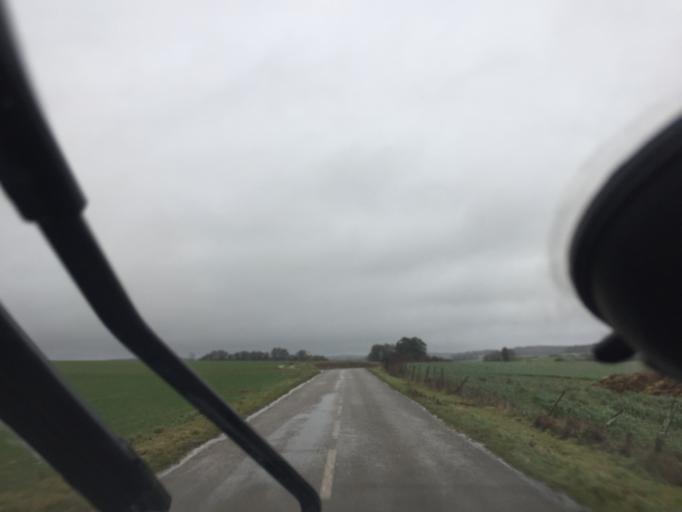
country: FR
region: Franche-Comte
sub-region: Departement du Jura
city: Orchamps
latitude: 47.1549
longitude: 5.6168
